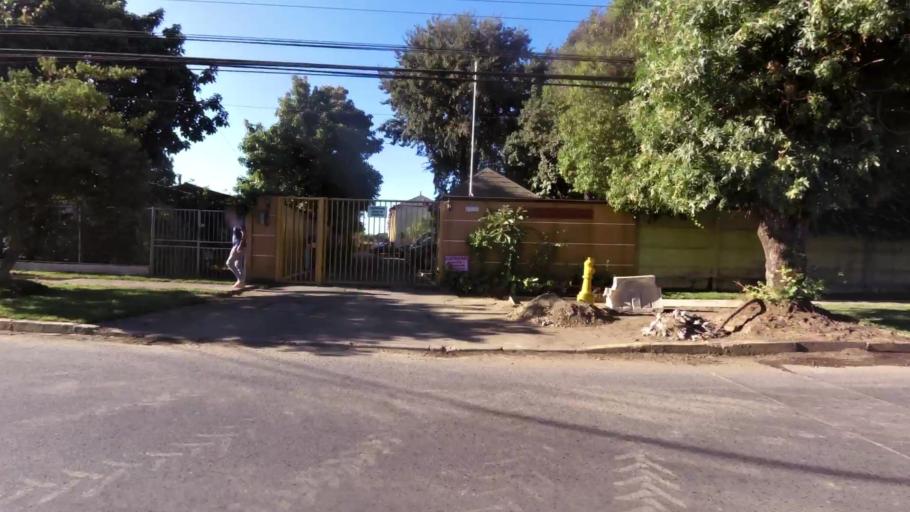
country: CL
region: Biobio
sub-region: Provincia de Concepcion
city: Concepcion
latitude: -36.8367
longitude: -73.1090
